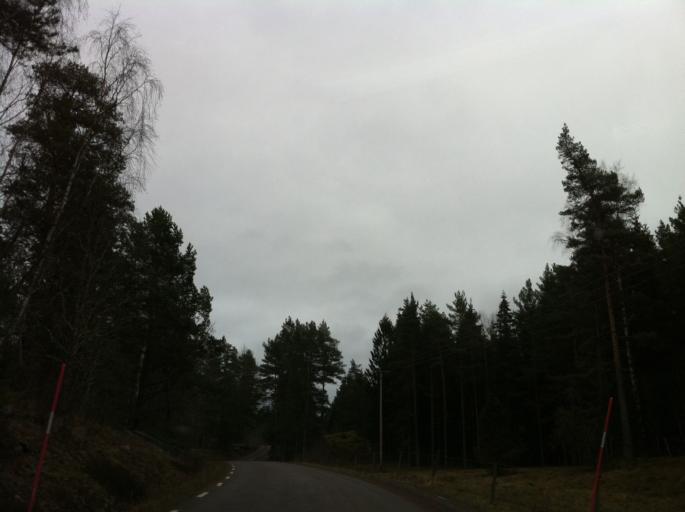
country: SE
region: Kalmar
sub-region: Vasterviks Kommun
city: Forserum
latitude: 57.9191
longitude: 16.6041
